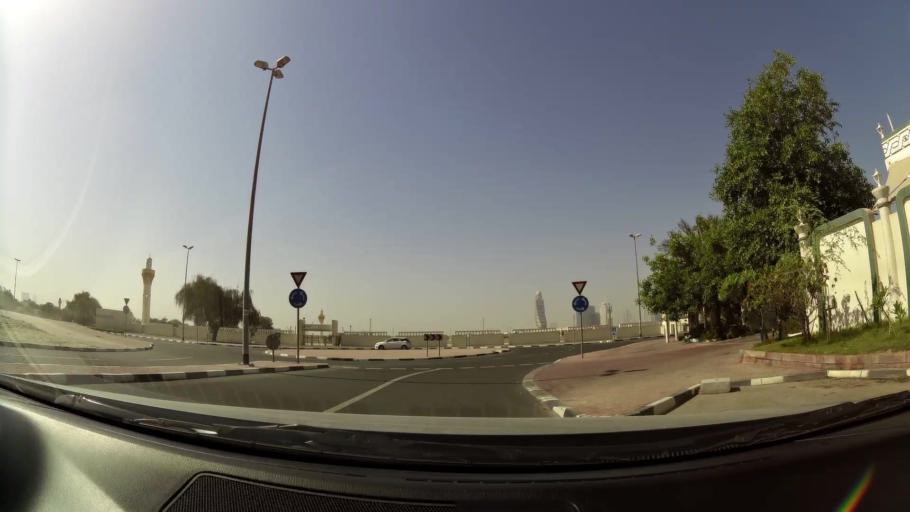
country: AE
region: Ash Shariqah
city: Sharjah
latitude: 25.2451
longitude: 55.2907
